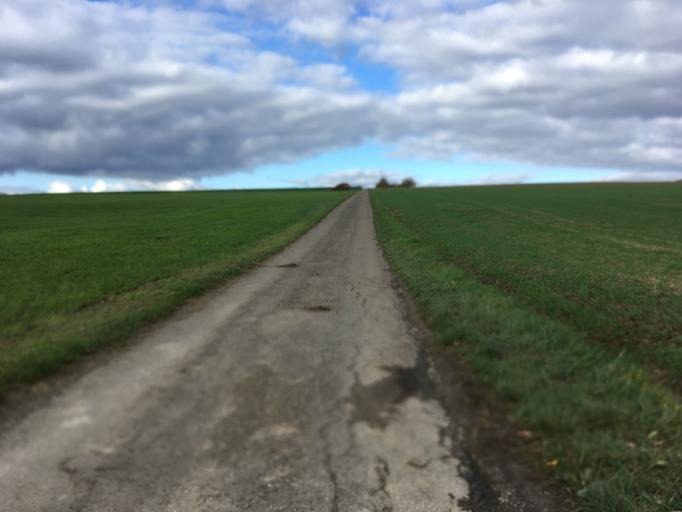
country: DE
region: Baden-Wuerttemberg
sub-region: Regierungsbezirk Stuttgart
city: Untermunkheim
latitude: 49.1943
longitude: 9.7407
